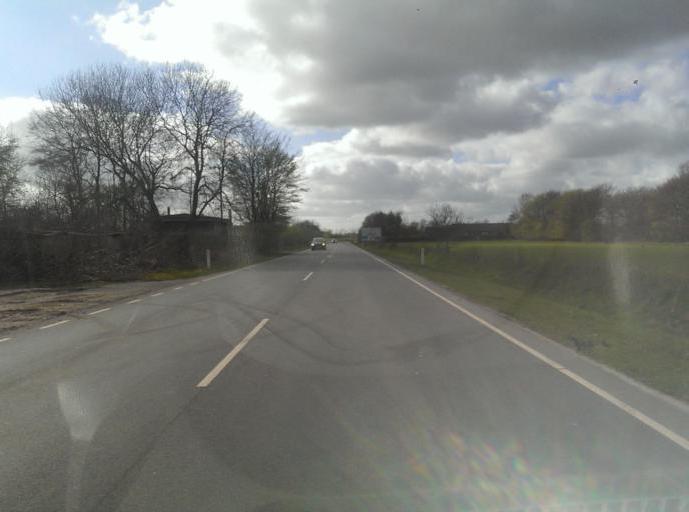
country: DK
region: South Denmark
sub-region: Esbjerg Kommune
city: Esbjerg
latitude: 55.5093
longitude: 8.5115
